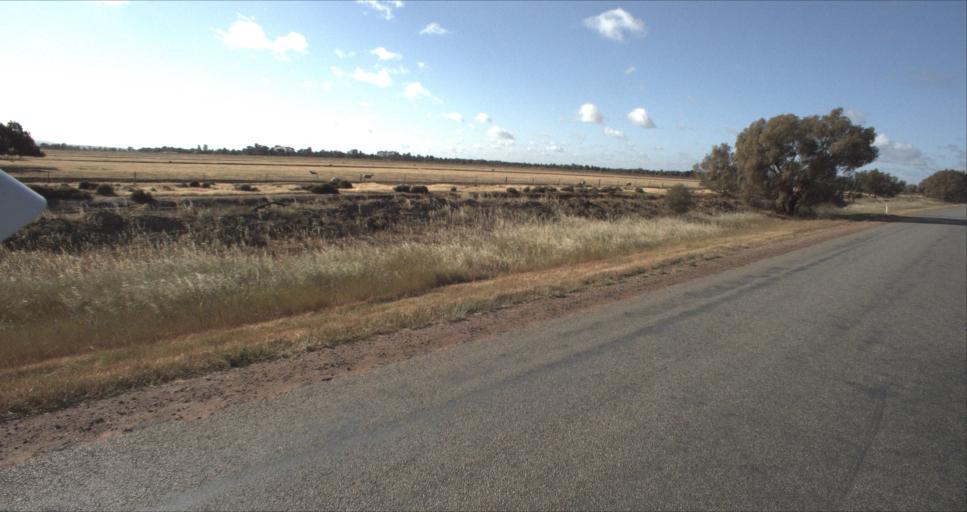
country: AU
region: New South Wales
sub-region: Leeton
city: Leeton
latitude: -34.5126
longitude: 146.3921
